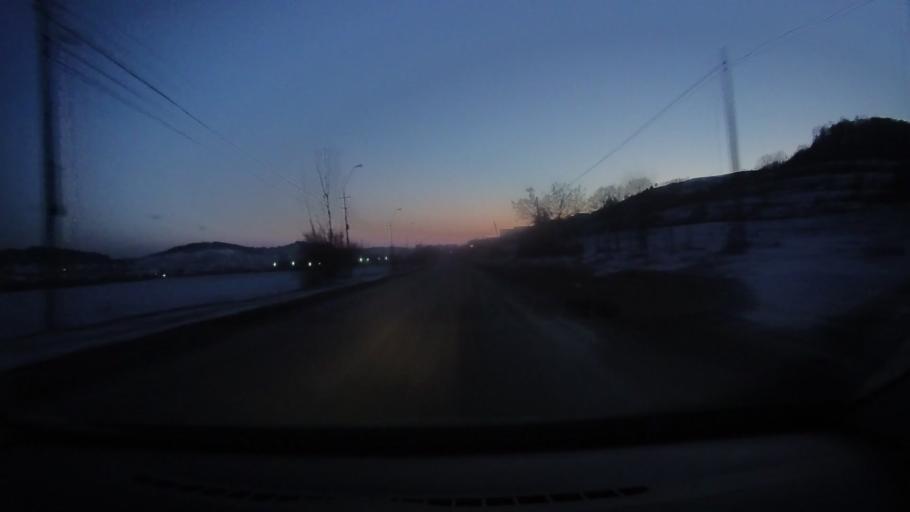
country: RO
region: Sibiu
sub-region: Municipiul Medias
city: Medias
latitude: 46.1784
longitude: 24.3668
